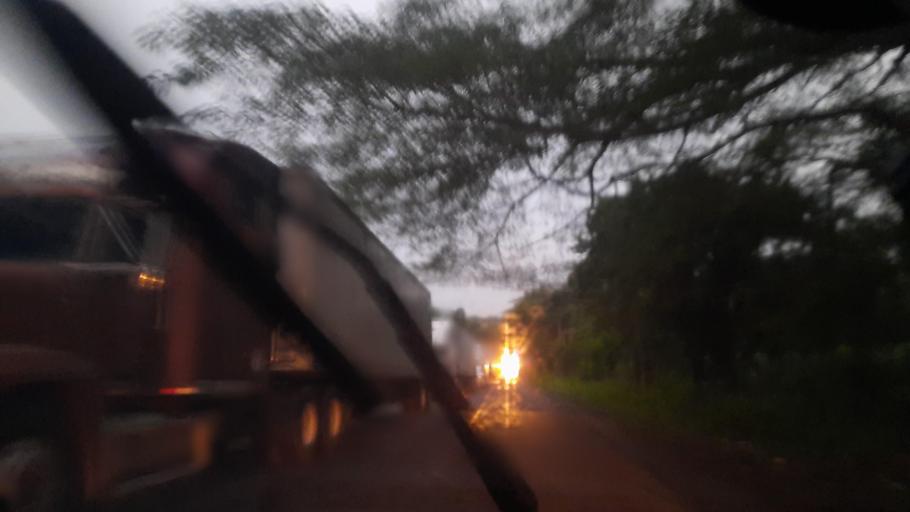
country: GT
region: Jutiapa
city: Atescatempa
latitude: 14.2144
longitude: -89.6855
